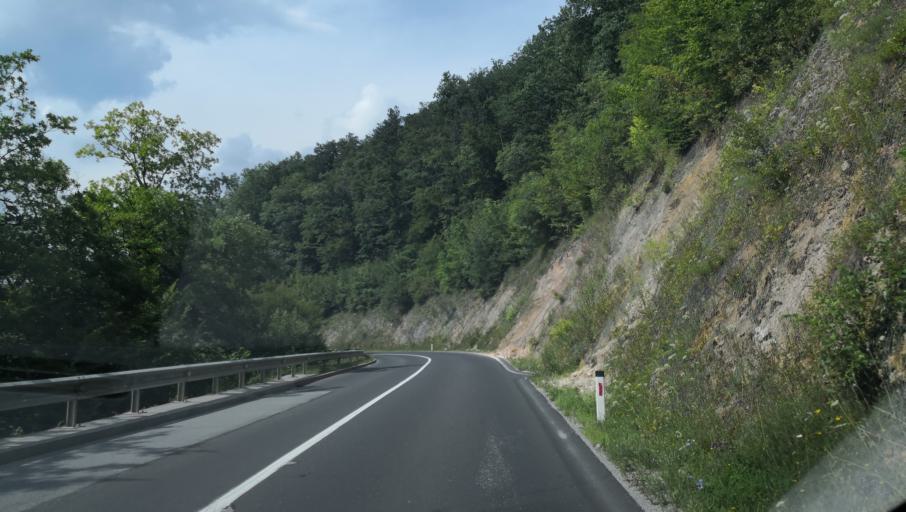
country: SI
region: Zuzemberk
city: Zuzemberk
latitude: 45.8448
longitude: 14.9061
